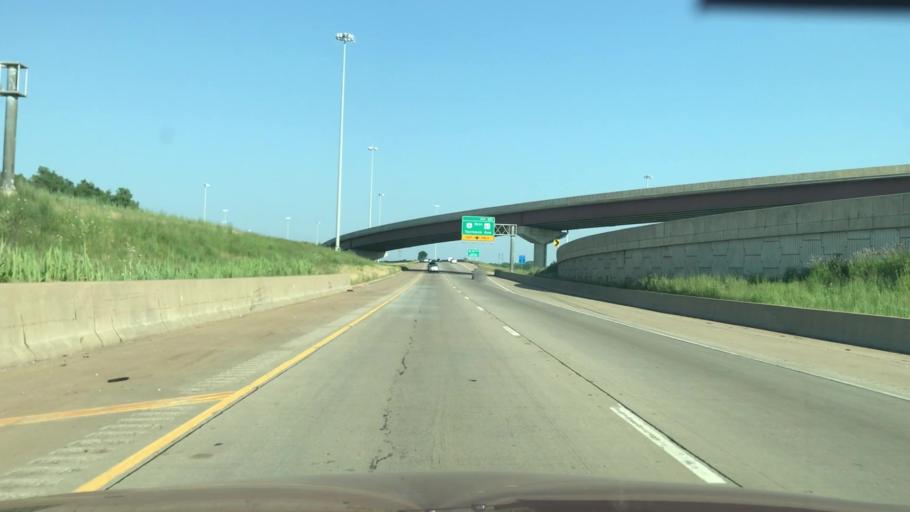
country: US
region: Illinois
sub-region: Cook County
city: Thornton
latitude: 41.5801
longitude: -87.5801
